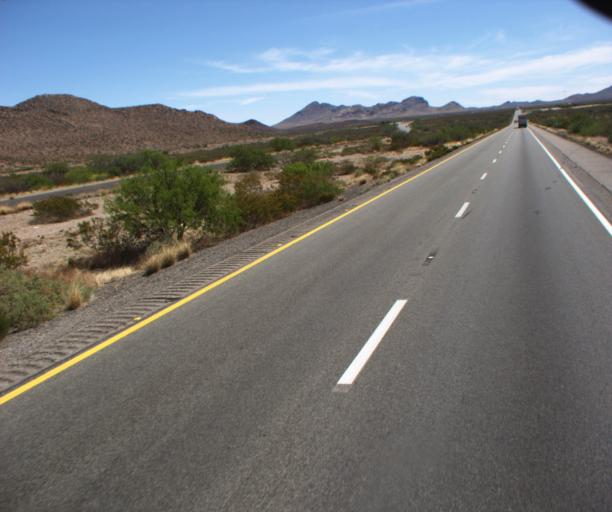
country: US
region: New Mexico
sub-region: Hidalgo County
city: Lordsburg
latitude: 32.2398
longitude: -109.1028
